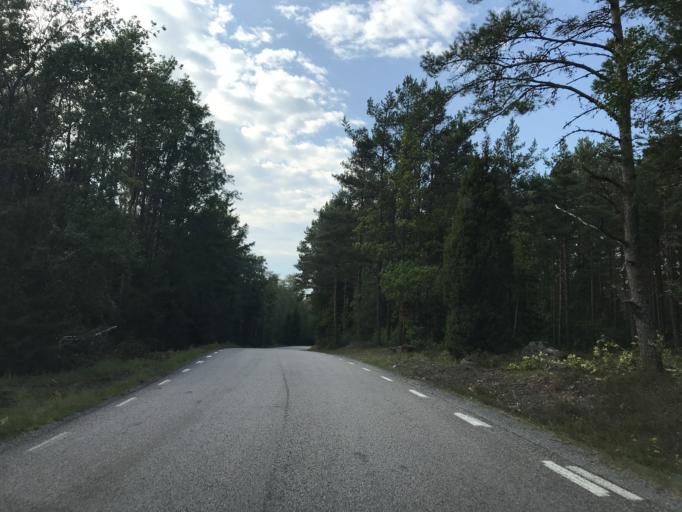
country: SE
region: Stockholm
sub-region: Norrtalje Kommun
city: Bjorko
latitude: 59.8814
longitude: 18.9818
